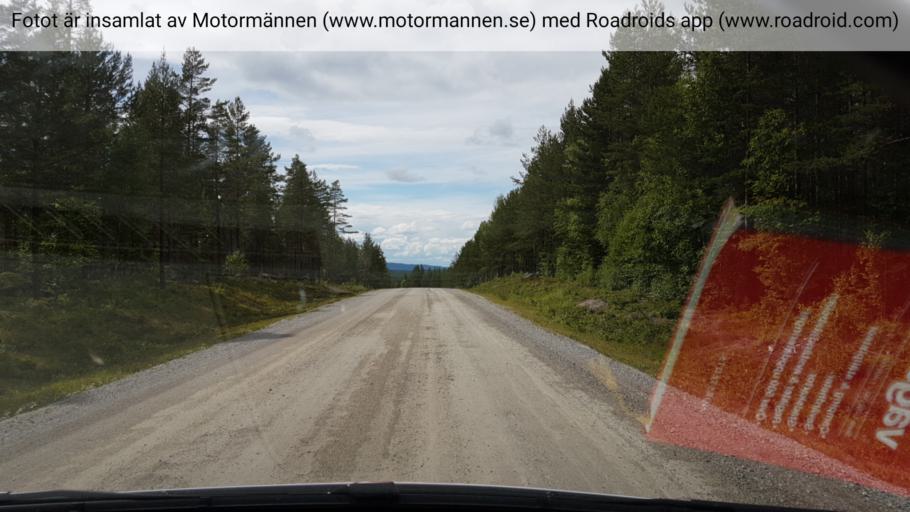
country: SE
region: Vaesternorrland
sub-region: Solleftea Kommun
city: Solleftea
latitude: 63.3245
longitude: 17.3528
